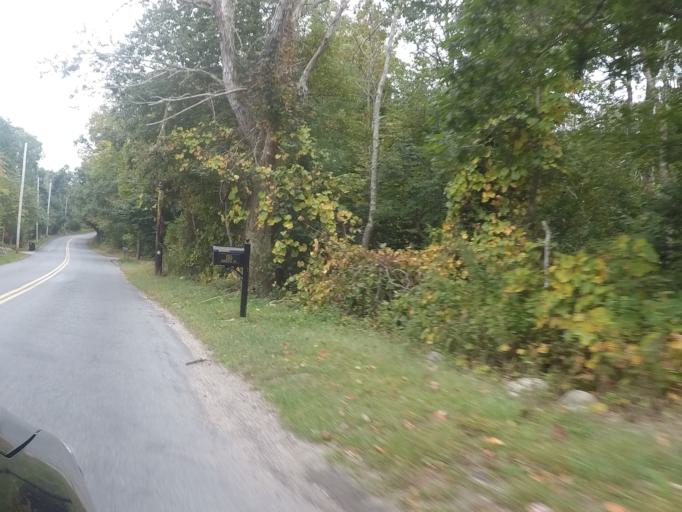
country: US
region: Massachusetts
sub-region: Bristol County
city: Smith Mills
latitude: 41.5627
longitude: -71.0075
